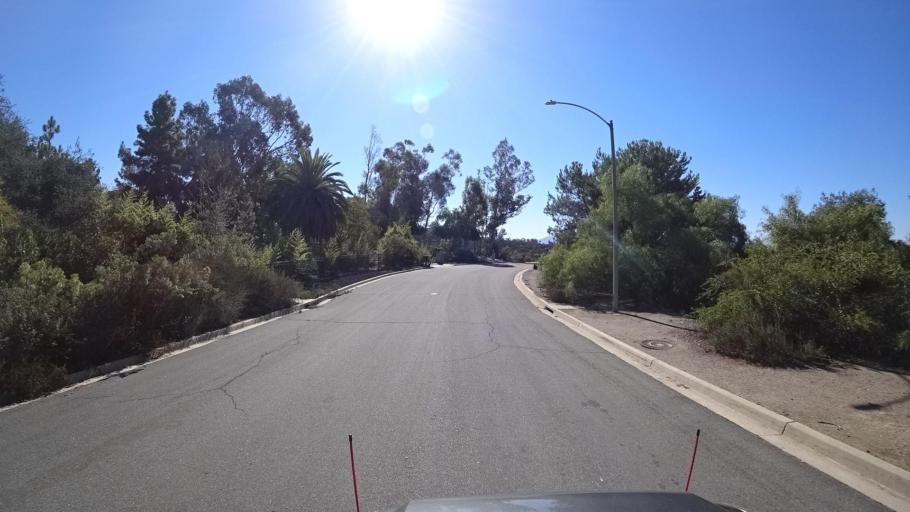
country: US
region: California
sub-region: San Diego County
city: Jamul
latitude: 32.7379
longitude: -116.8600
